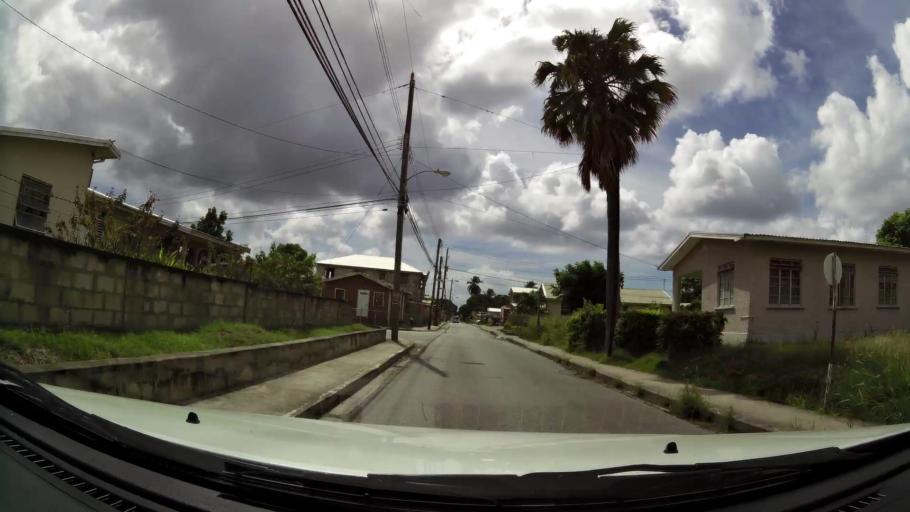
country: BB
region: Saint Michael
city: Bridgetown
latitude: 13.1218
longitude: -59.6164
